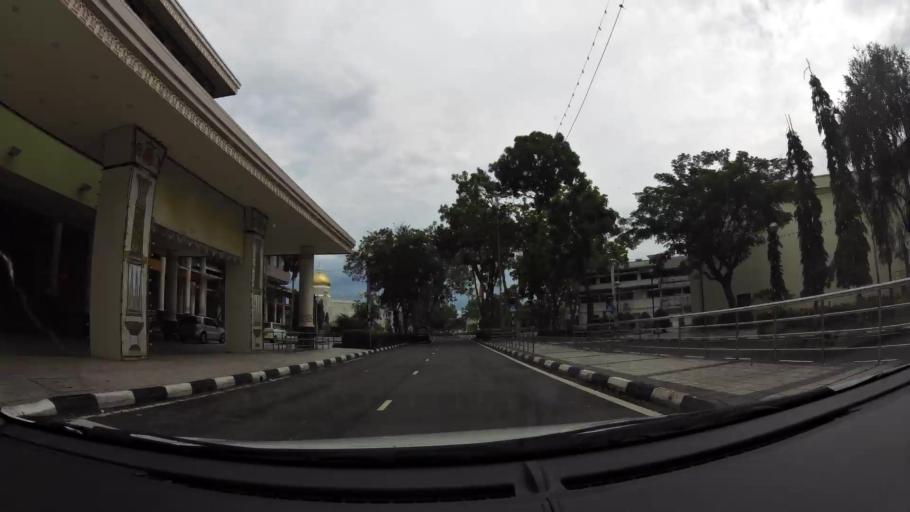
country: BN
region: Brunei and Muara
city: Bandar Seri Begawan
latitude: 4.8878
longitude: 114.9413
